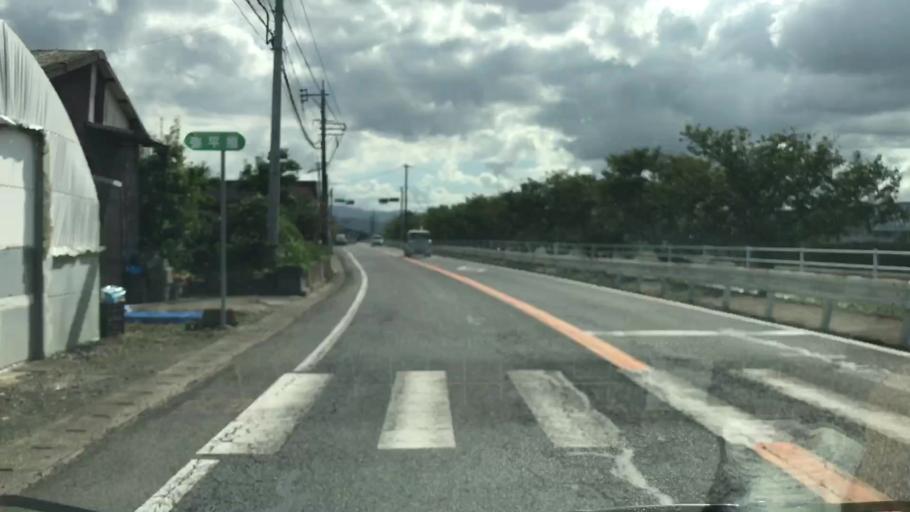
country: JP
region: Saga Prefecture
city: Kashima
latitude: 33.1606
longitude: 130.1646
